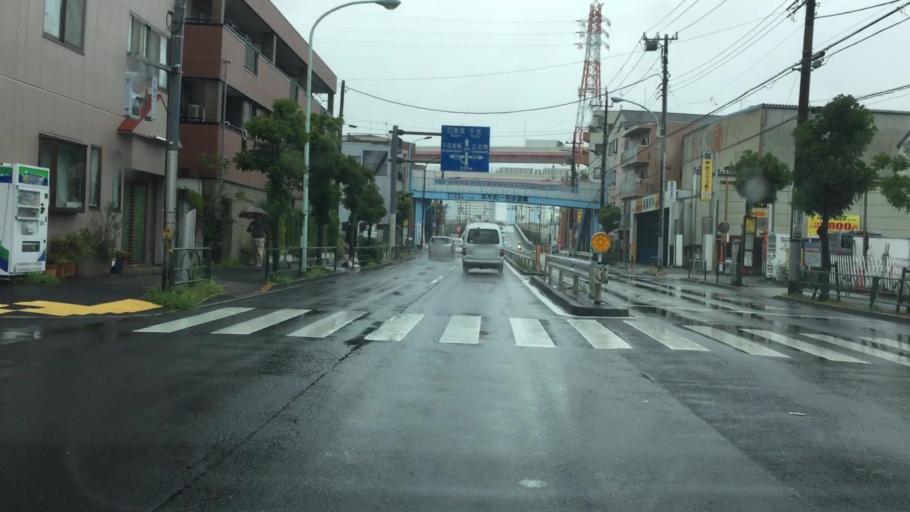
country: JP
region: Saitama
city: Soka
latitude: 35.7632
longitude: 139.7874
